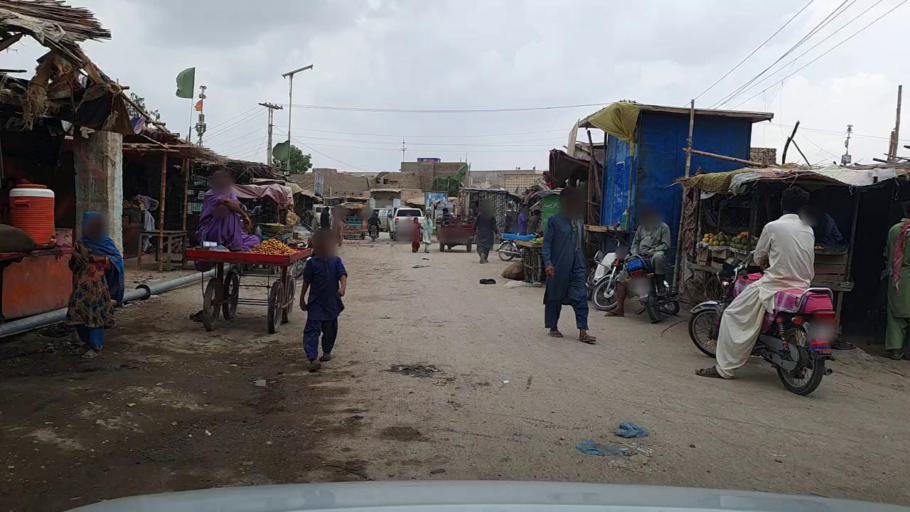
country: PK
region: Sindh
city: Sehwan
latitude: 26.3408
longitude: 67.7212
